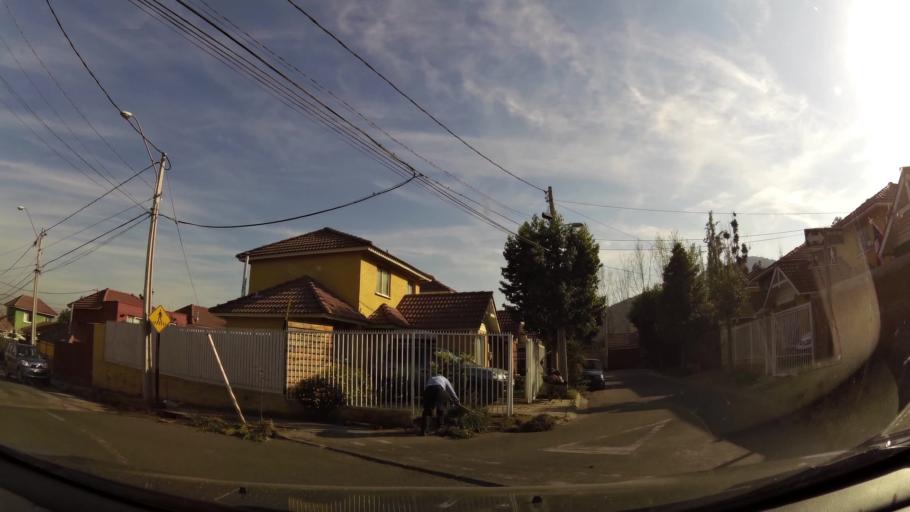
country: CL
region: Santiago Metropolitan
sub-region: Provincia de Cordillera
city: Puente Alto
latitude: -33.5592
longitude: -70.5428
